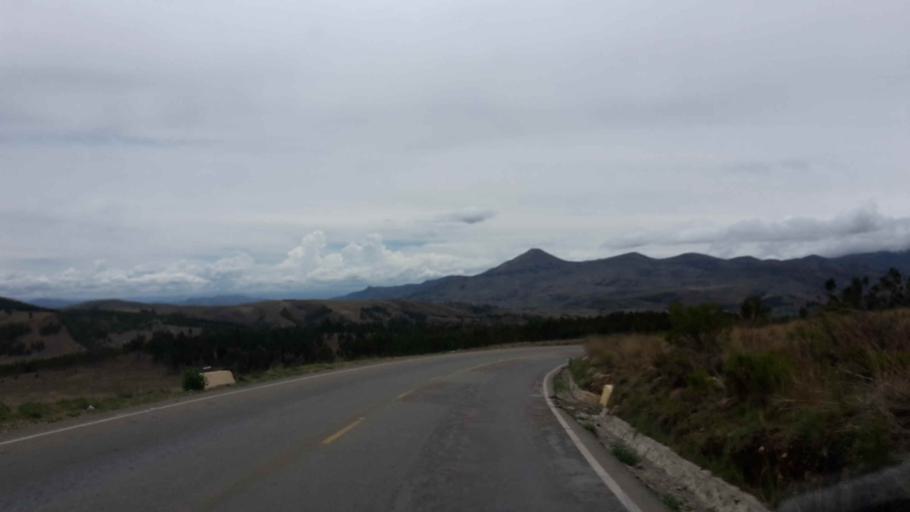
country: BO
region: Cochabamba
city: Arani
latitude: -17.4651
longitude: -65.6953
